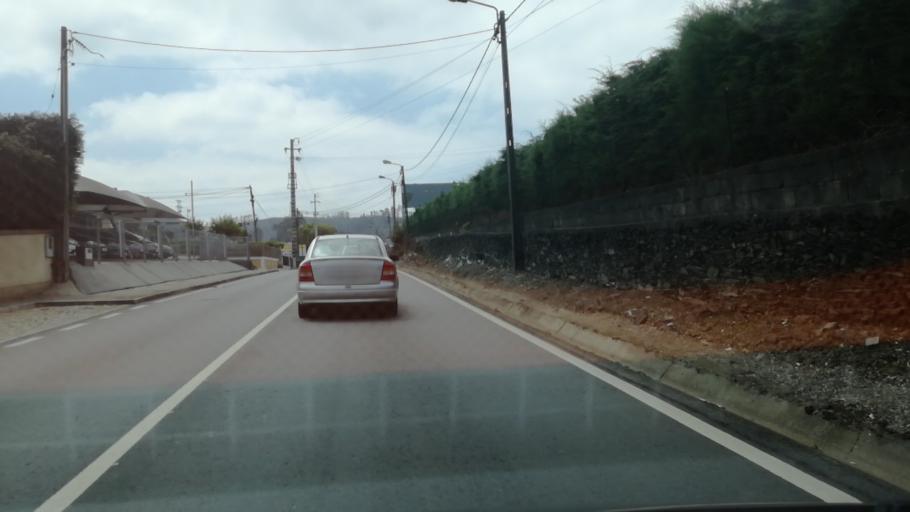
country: PT
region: Porto
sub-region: Trofa
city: Sao Romao do Coronado
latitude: 41.3138
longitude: -8.5808
